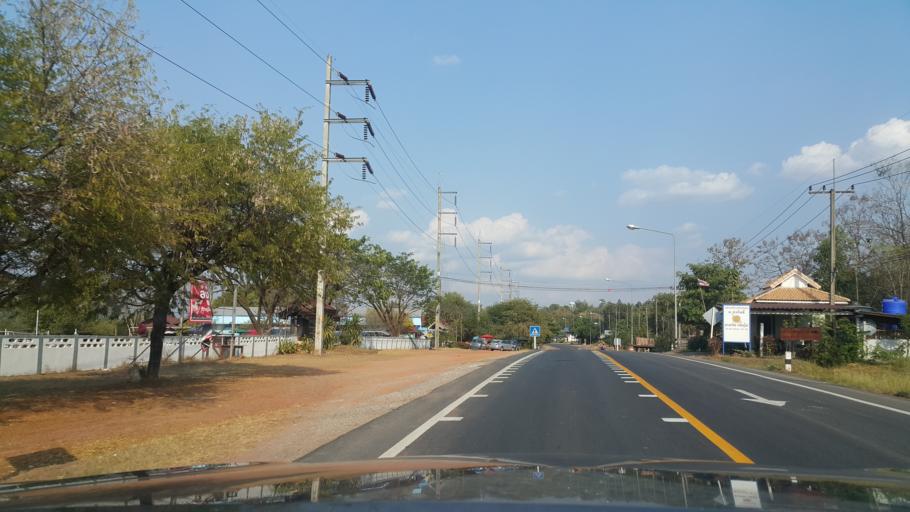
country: TH
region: Phitsanulok
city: Nakhon Thai
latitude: 17.1590
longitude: 100.9632
